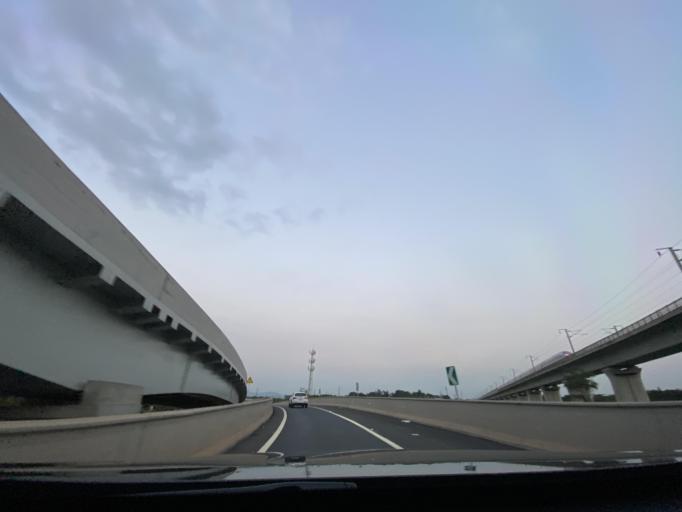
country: CN
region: Sichuan
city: Chengdu
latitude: 30.5709
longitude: 104.1369
